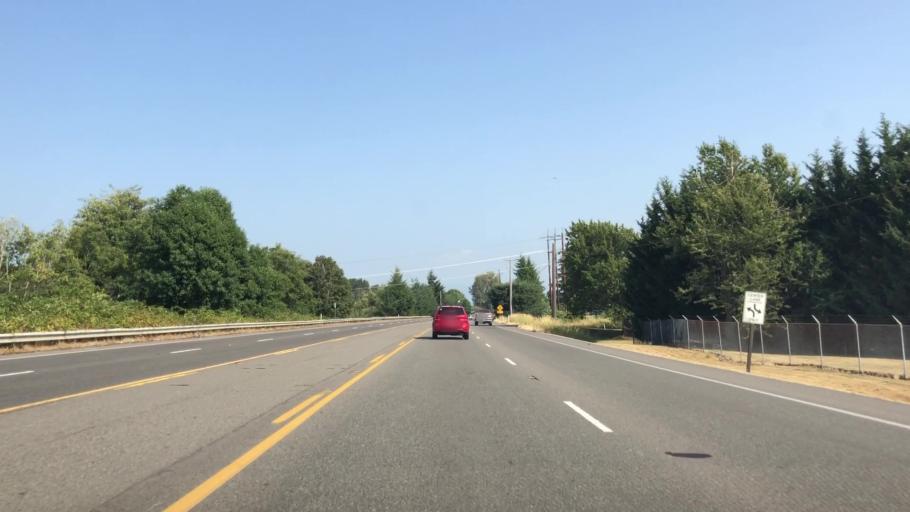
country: US
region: Washington
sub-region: Pierce County
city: Fife
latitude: 47.2229
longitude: -122.3593
